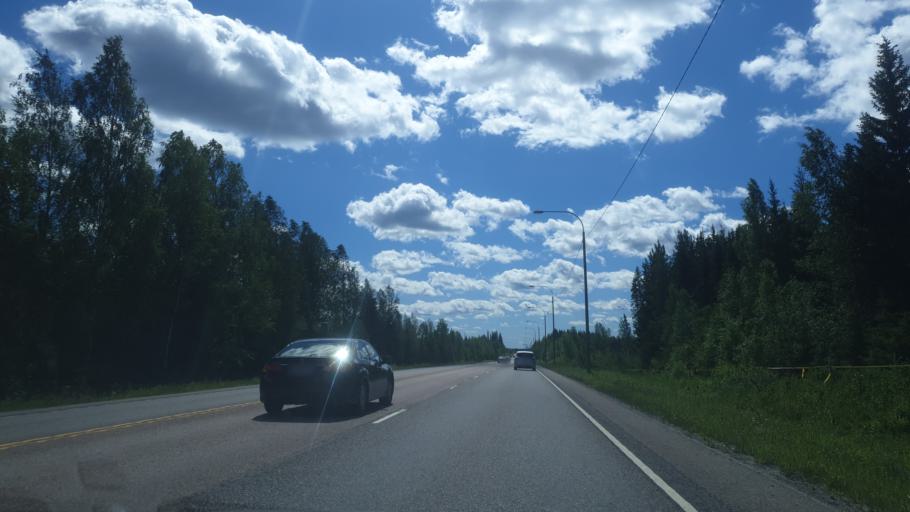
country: FI
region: Northern Savo
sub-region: Varkaus
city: Varkaus
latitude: 62.3799
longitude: 27.8093
